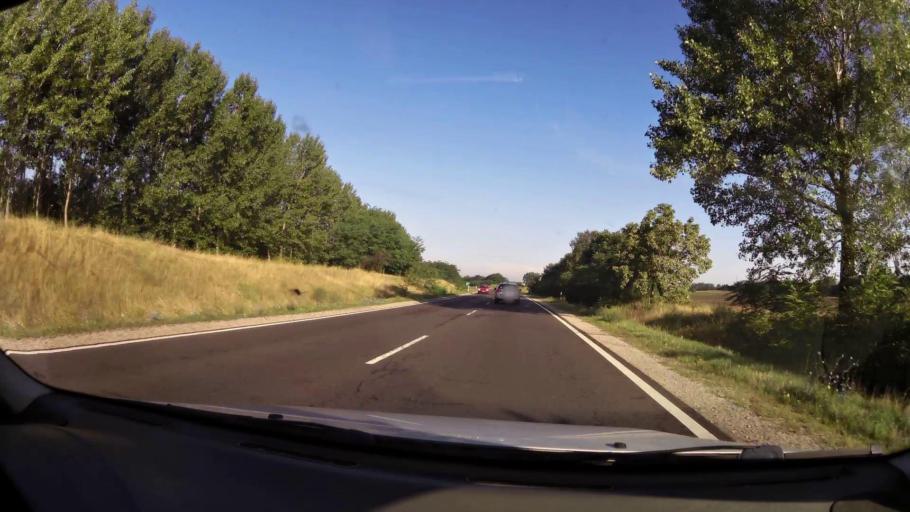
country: HU
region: Pest
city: Albertirsa
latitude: 47.2610
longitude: 19.6200
